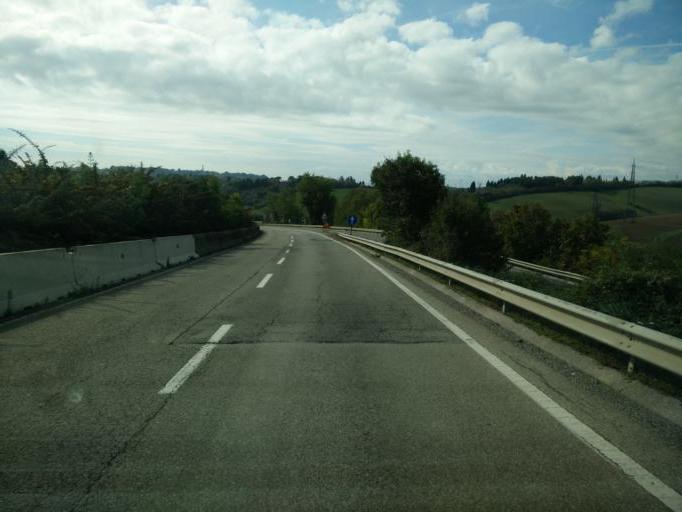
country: IT
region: Tuscany
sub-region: Provincia di Siena
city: Belverde
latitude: 43.3361
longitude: 11.2921
